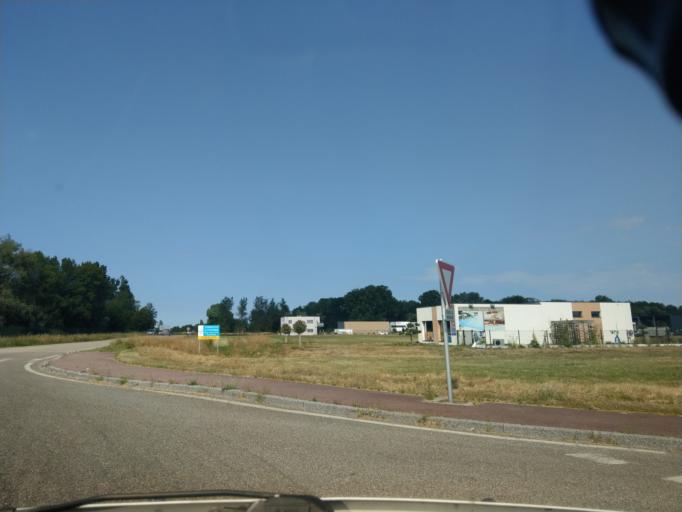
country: FR
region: Alsace
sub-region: Departement du Bas-Rhin
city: Roppenheim
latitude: 48.8187
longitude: 8.0200
